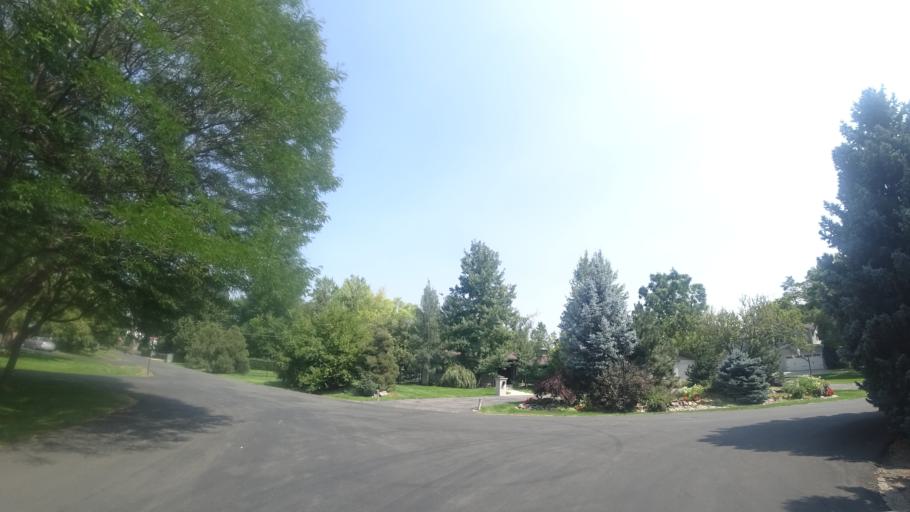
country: US
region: Colorado
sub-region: Arapahoe County
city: Cherry Hills Village
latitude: 39.6267
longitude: -104.9753
